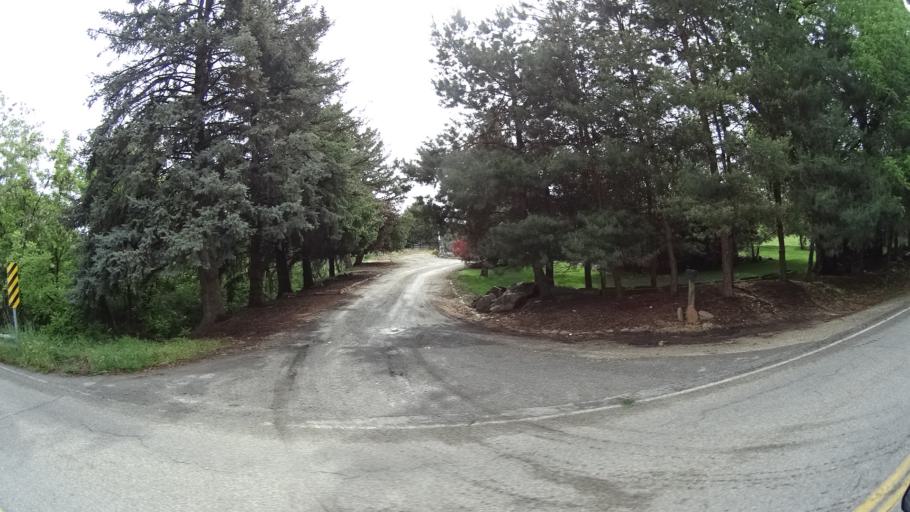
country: US
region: Idaho
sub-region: Ada County
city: Eagle
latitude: 43.7027
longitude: -116.3791
